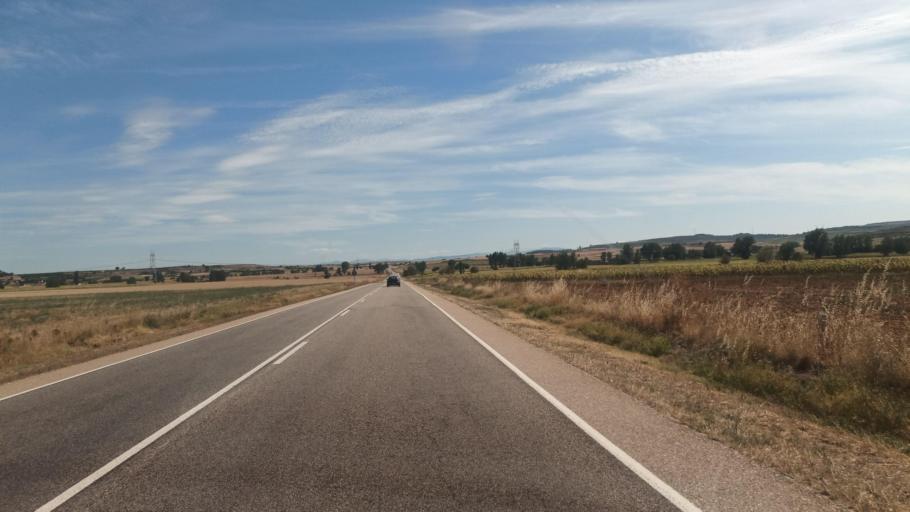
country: ES
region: Castille and Leon
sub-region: Provincia de Burgos
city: Aguilar de Bureba
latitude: 42.5972
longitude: -3.3464
